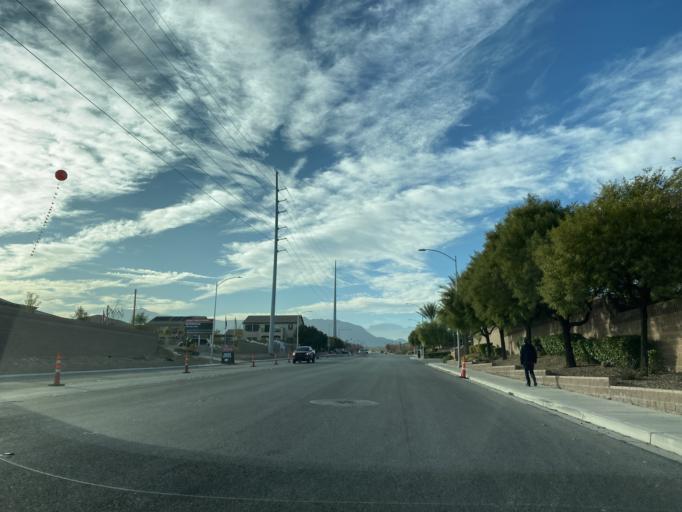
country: US
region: Nevada
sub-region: Clark County
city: Summerlin South
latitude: 36.2995
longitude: -115.3124
